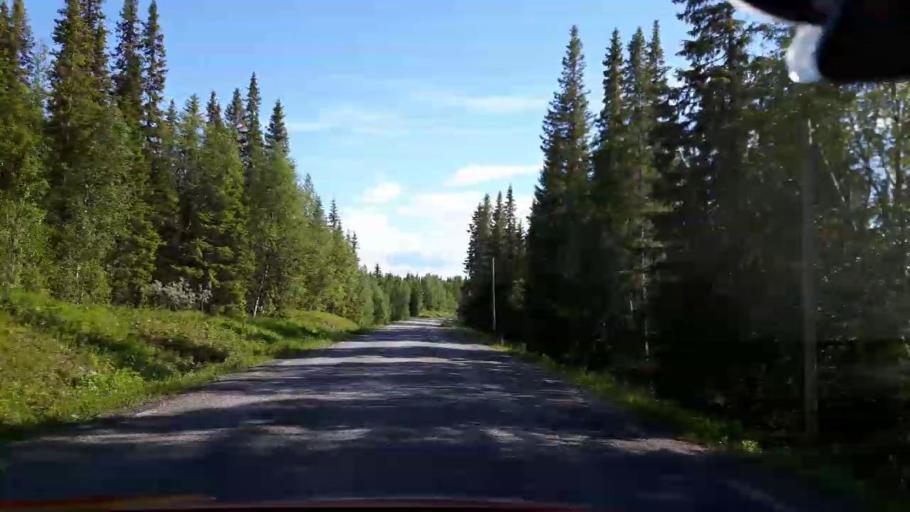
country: SE
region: Jaemtland
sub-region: Krokoms Kommun
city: Valla
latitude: 63.7442
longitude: 14.1193
